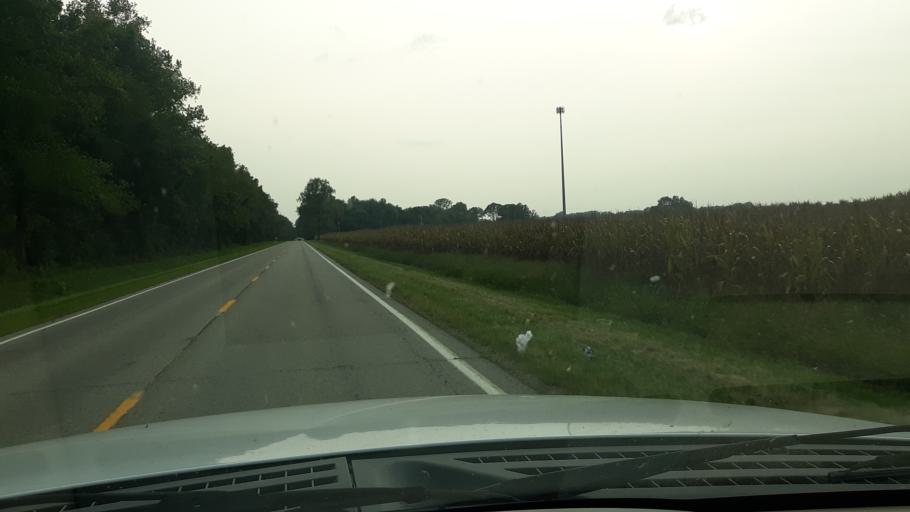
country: US
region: Illinois
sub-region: Edwards County
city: Grayville
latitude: 38.3197
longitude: -87.9229
